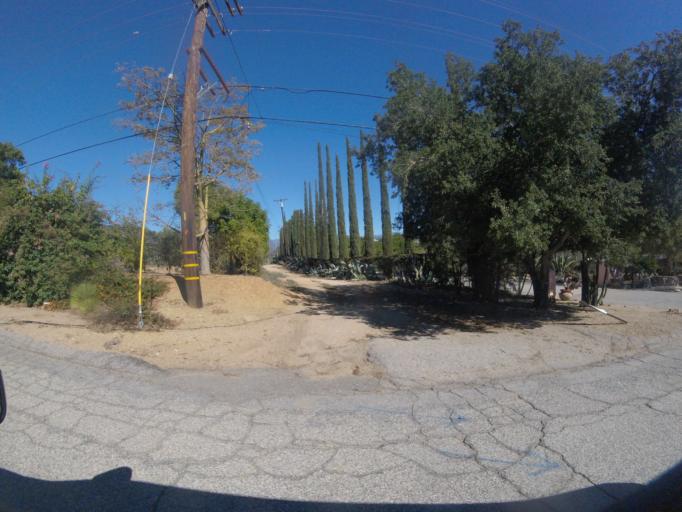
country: US
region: California
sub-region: San Bernardino County
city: Mentone
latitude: 34.0213
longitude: -117.1201
